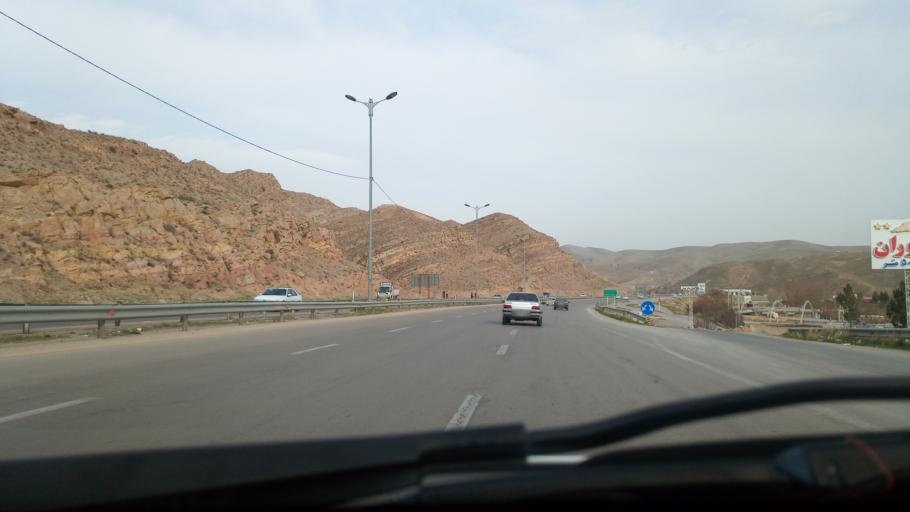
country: IR
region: Khorasan-e Shomali
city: Bojnurd
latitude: 37.4788
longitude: 57.4180
